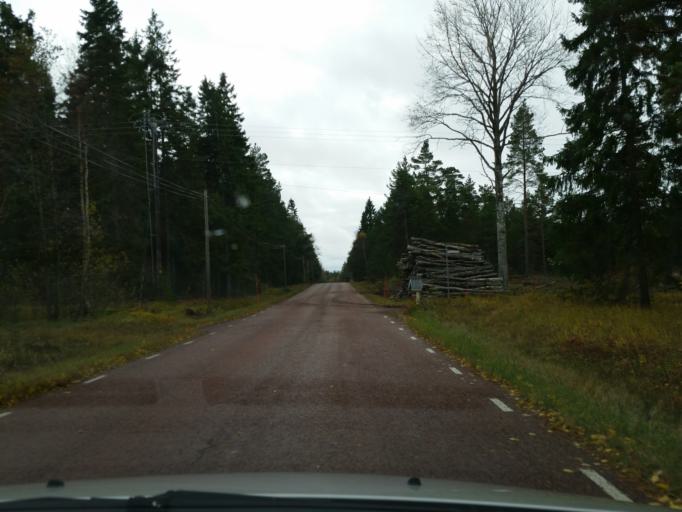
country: AX
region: Alands landsbygd
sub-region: Lemland
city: Lemland
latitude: 60.0042
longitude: 20.1869
